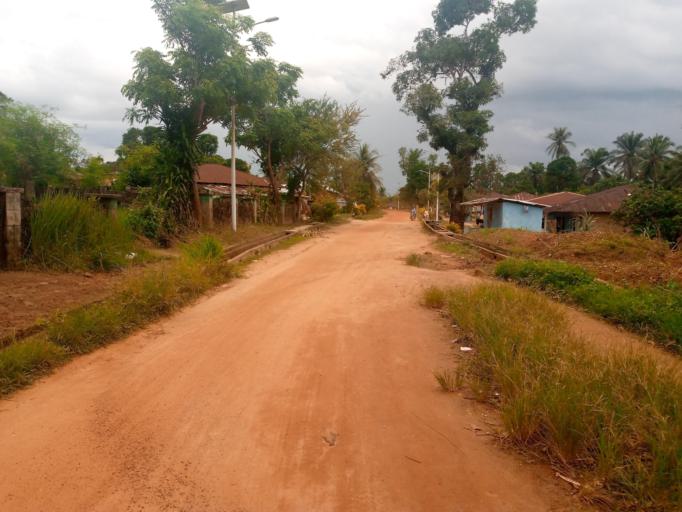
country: SL
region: Southern Province
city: Mogbwemo
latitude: 7.6060
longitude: -12.1733
